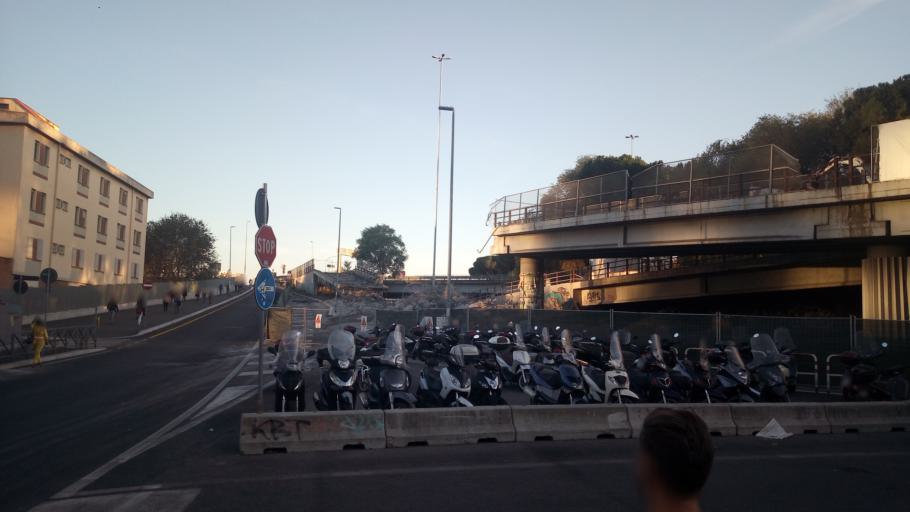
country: IT
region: Latium
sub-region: Citta metropolitana di Roma Capitale
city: Rome
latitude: 41.9095
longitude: 12.5310
